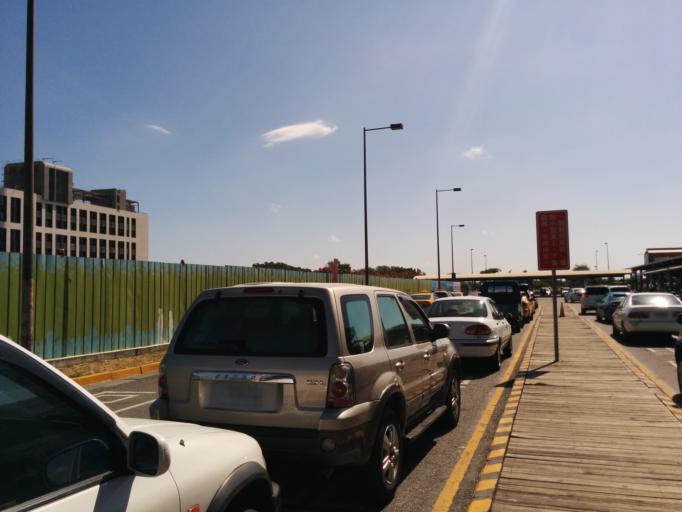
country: TW
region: Taiwan
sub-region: Taitung
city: Taitung
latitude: 22.7938
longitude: 121.1233
